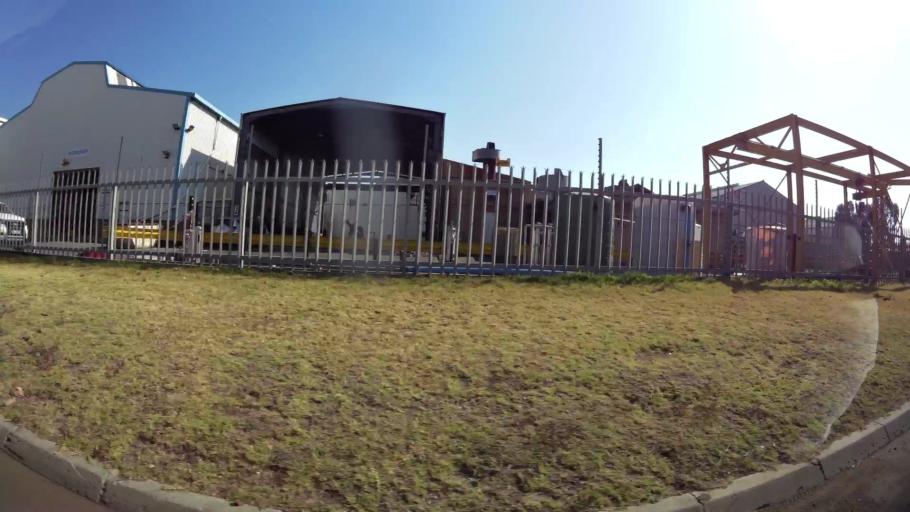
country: ZA
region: Gauteng
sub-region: Ekurhuleni Metropolitan Municipality
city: Boksburg
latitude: -26.1577
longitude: 28.2142
